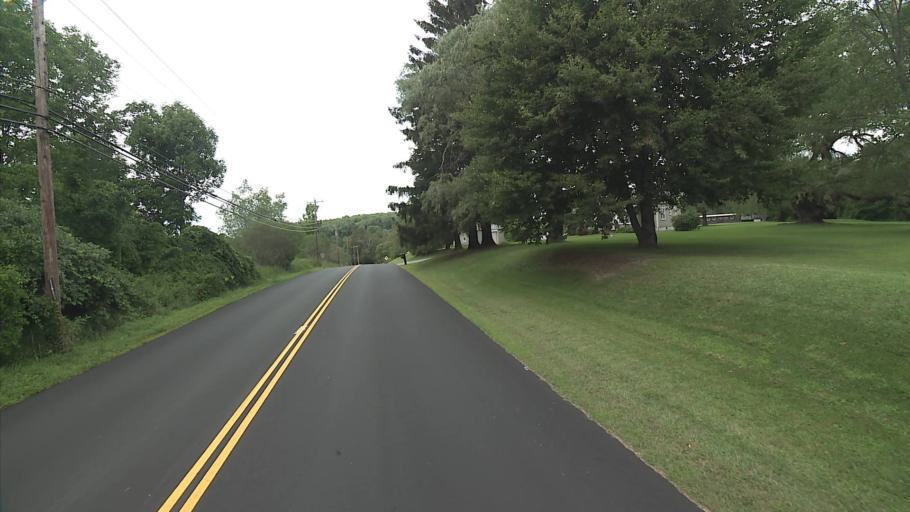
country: US
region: Connecticut
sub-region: Windham County
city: South Woodstock
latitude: 41.9511
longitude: -72.0289
